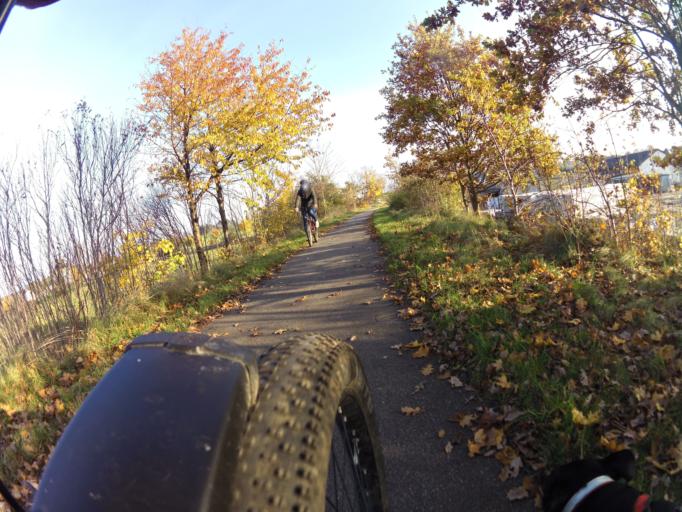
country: PL
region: Pomeranian Voivodeship
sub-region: Powiat pucki
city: Krokowa
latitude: 54.7830
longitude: 18.1687
